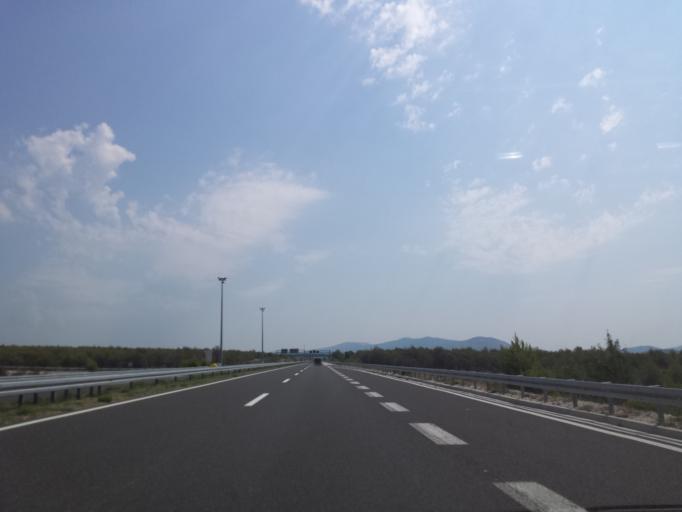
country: HR
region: Sibensko-Kniniska
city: Zaton
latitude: 43.8360
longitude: 15.8876
